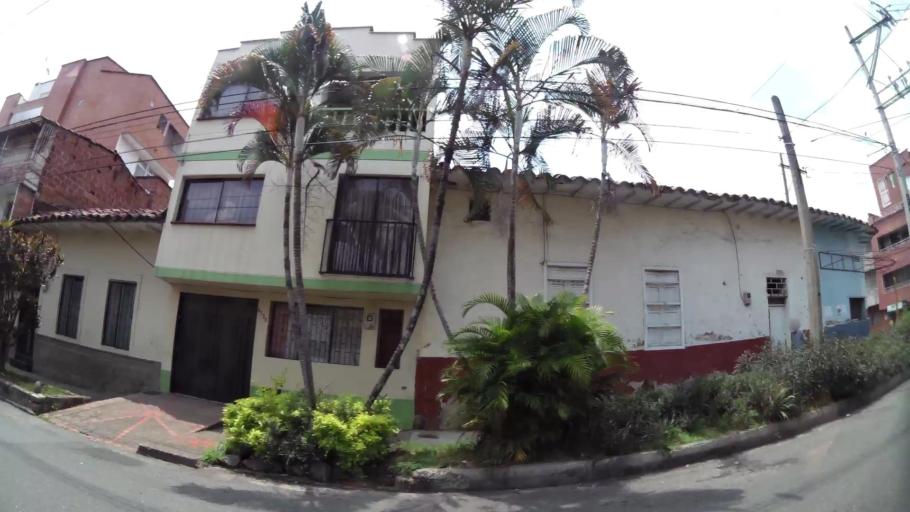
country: CO
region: Antioquia
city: Medellin
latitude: 6.2471
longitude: -75.6104
